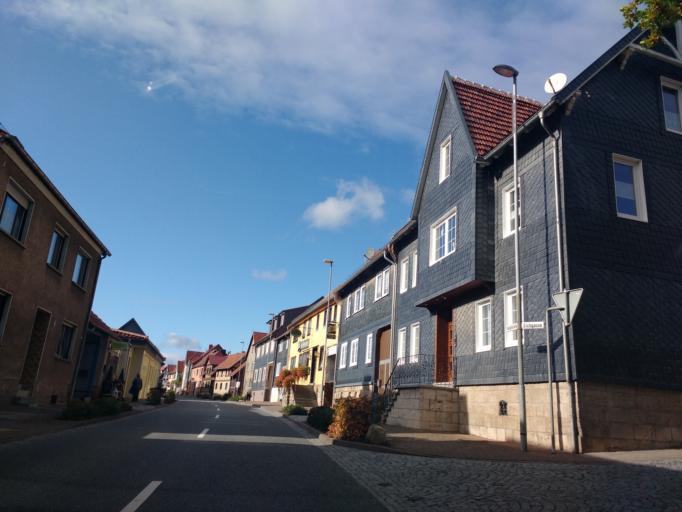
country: DE
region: Thuringia
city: Kirchworbis
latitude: 51.4114
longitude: 10.3983
